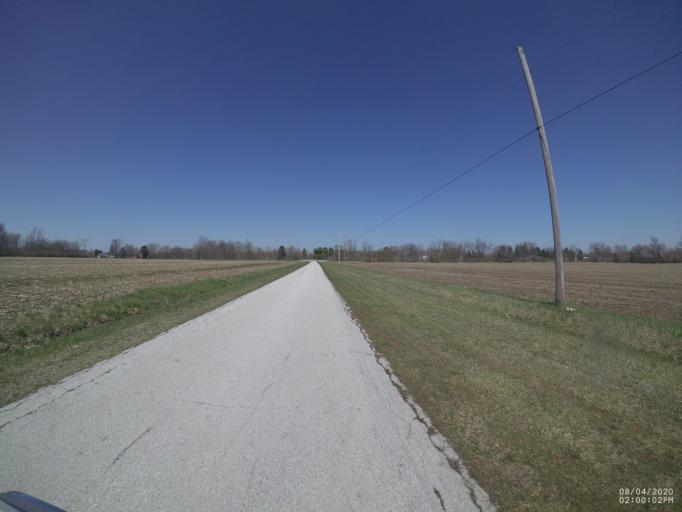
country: US
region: Ohio
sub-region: Sandusky County
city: Gibsonburg
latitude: 41.3094
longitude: -83.2835
